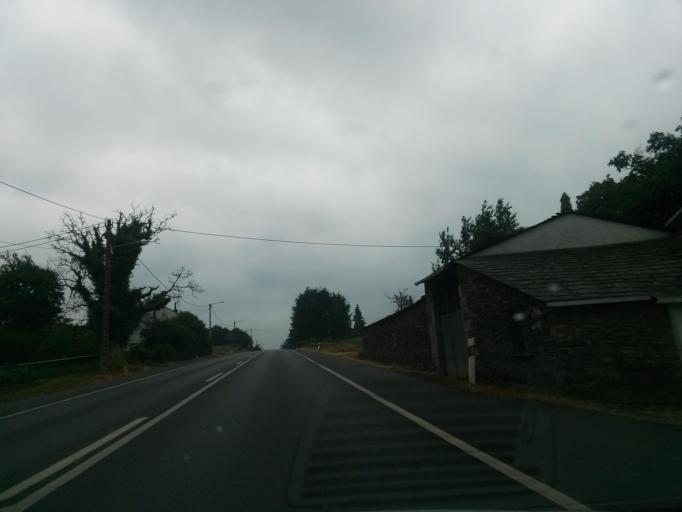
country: ES
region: Galicia
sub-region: Provincia de Lugo
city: Begonte
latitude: 43.1338
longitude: -7.6558
